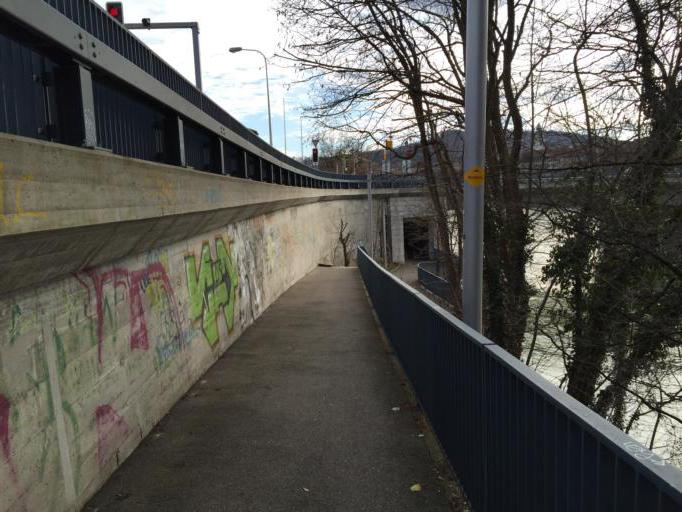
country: CH
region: Solothurn
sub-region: Bezirk Olten
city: Olten
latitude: 47.3525
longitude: 7.9067
